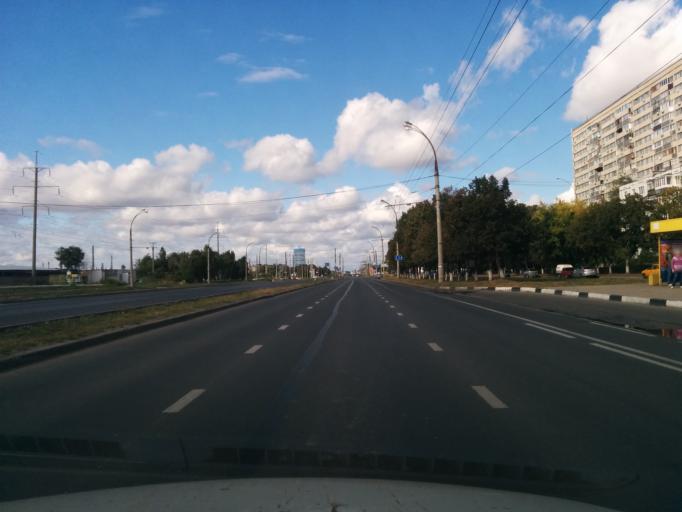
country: RU
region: Samara
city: Tol'yatti
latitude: 53.5370
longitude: 49.2634
